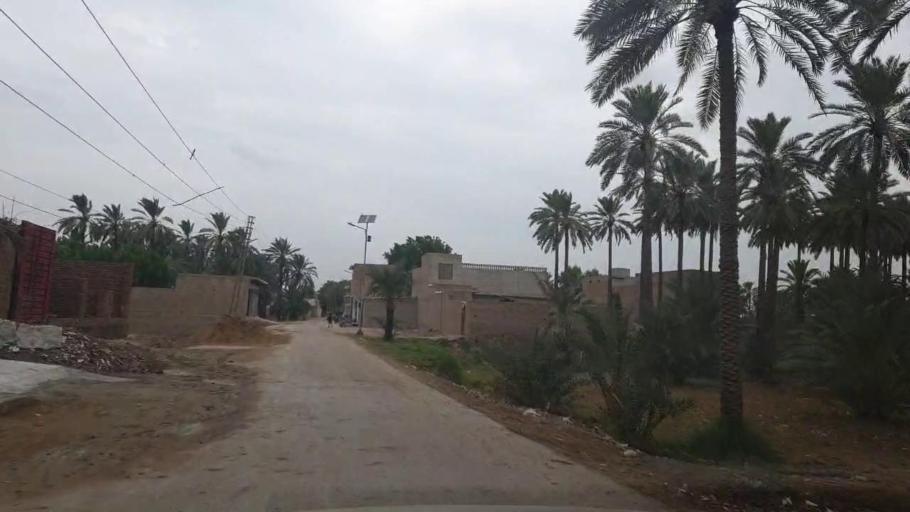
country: PK
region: Sindh
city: Khairpur
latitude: 27.5494
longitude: 68.7509
